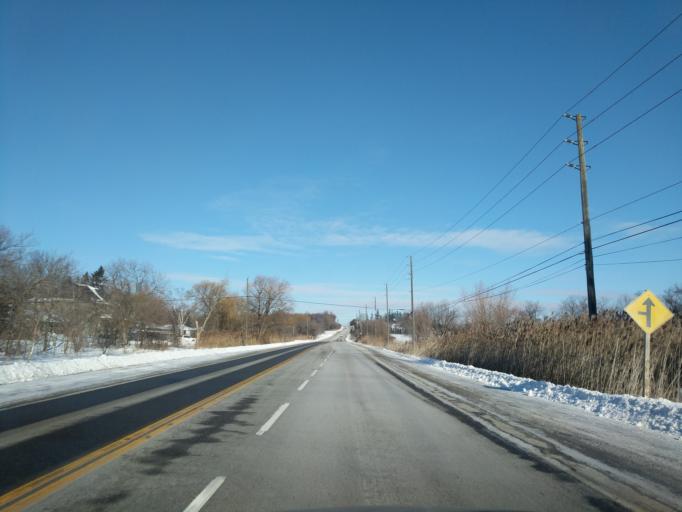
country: CA
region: Ontario
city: Pickering
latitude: 43.8469
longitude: -79.1496
